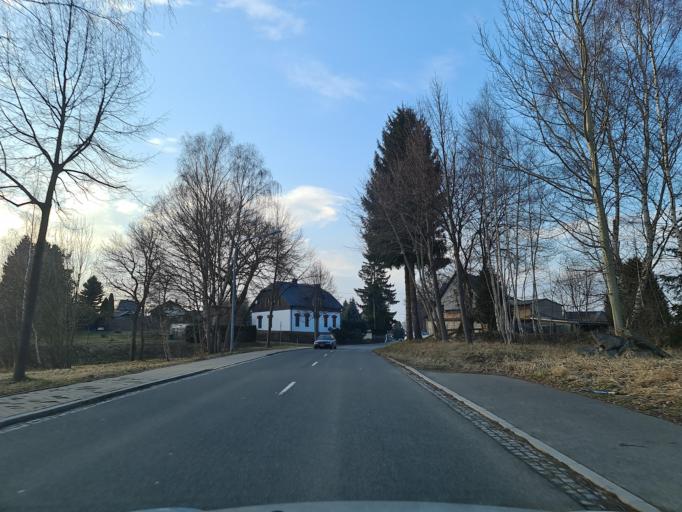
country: DE
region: Saxony
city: Auerbach
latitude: 50.5072
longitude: 12.4251
